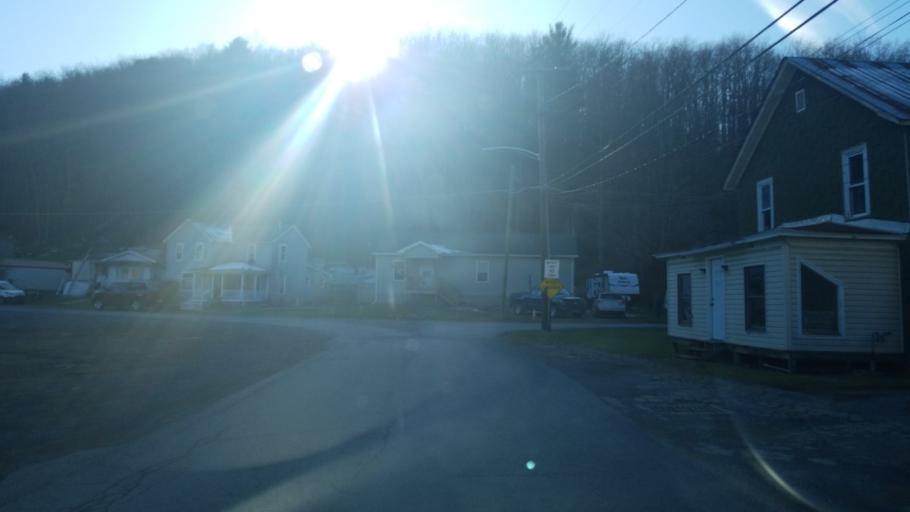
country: US
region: Pennsylvania
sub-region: Potter County
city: Coudersport
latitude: 41.6304
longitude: -78.0944
